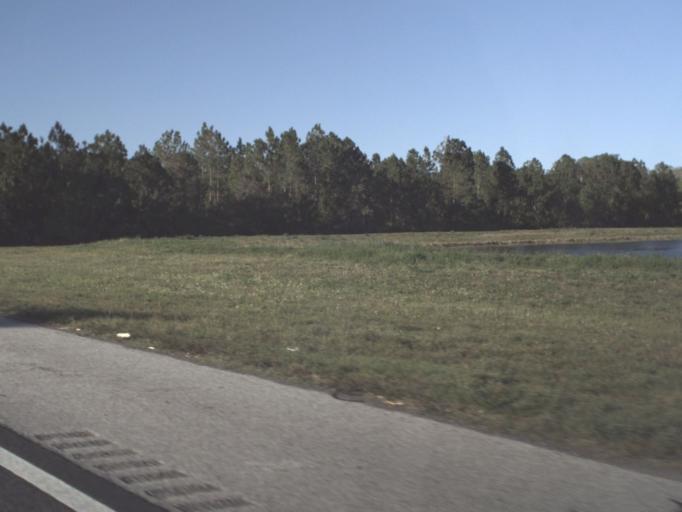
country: US
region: Florida
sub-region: Flagler County
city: Flagler Beach
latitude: 29.4856
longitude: -81.1873
